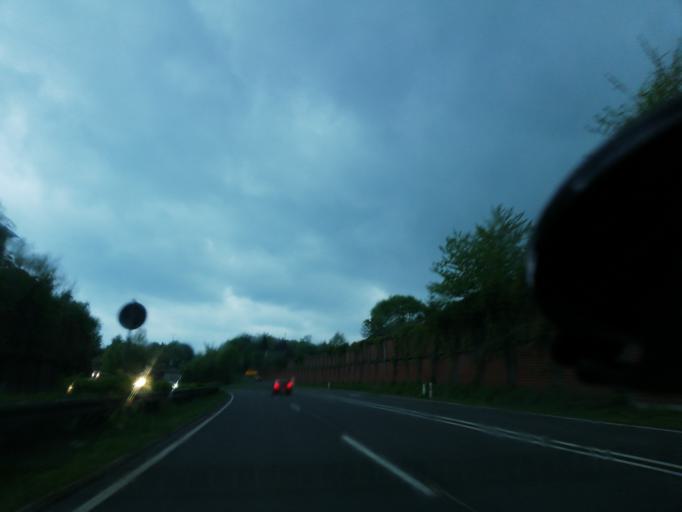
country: DE
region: North Rhine-Westphalia
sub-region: Regierungsbezirk Dusseldorf
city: Wuppertal
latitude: 51.2370
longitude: 7.1589
